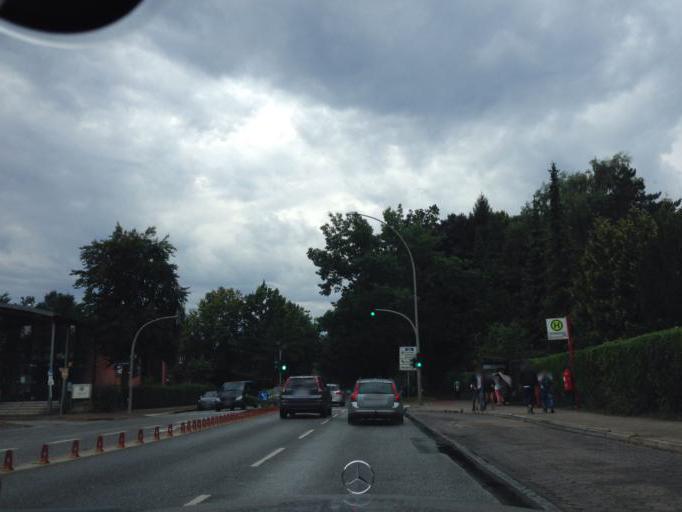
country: DE
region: Hamburg
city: Wellingsbuettel
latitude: 53.6419
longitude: 10.0974
